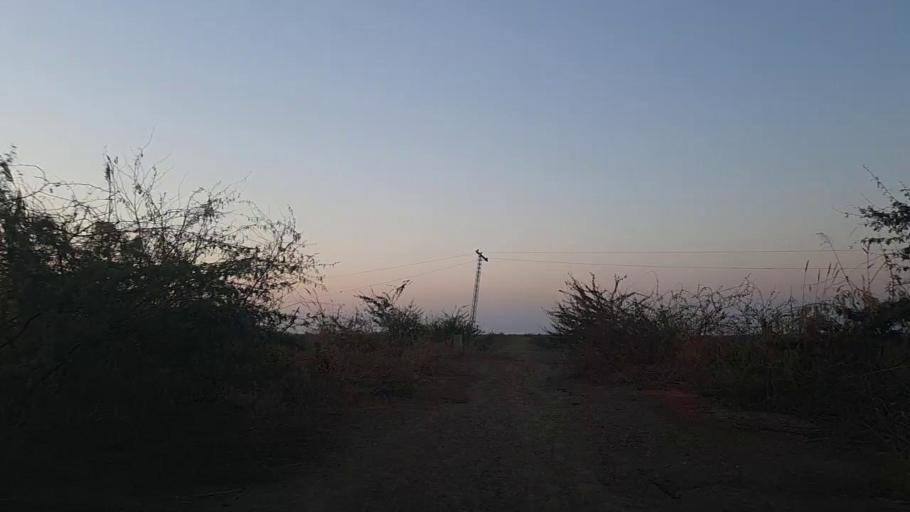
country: PK
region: Sindh
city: Tando Mittha Khan
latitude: 26.0683
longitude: 69.1590
